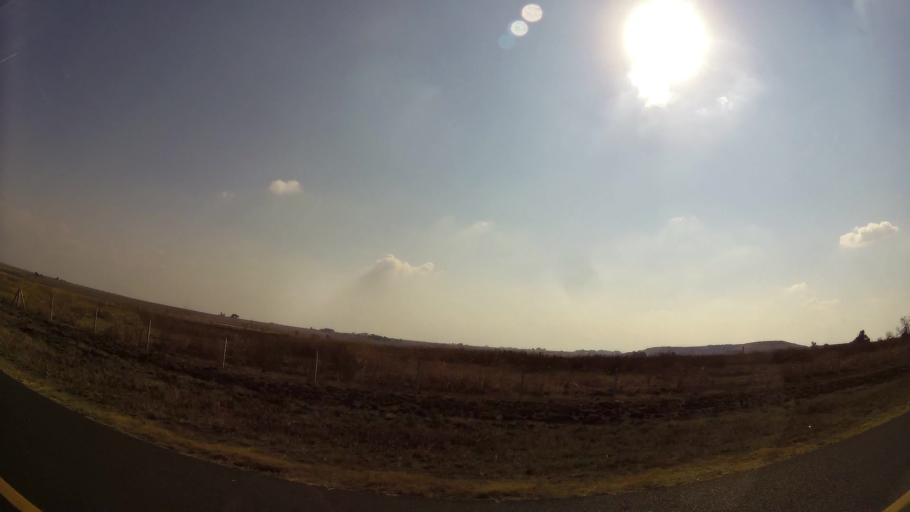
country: ZA
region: Gauteng
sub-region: Ekurhuleni Metropolitan Municipality
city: Springs
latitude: -26.1625
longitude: 28.5149
